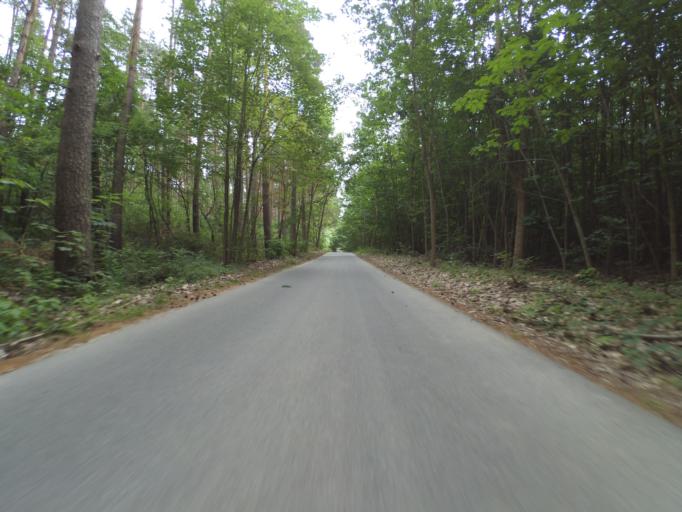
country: DE
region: Mecklenburg-Vorpommern
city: Grabowhofe
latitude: 53.5223
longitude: 12.6015
